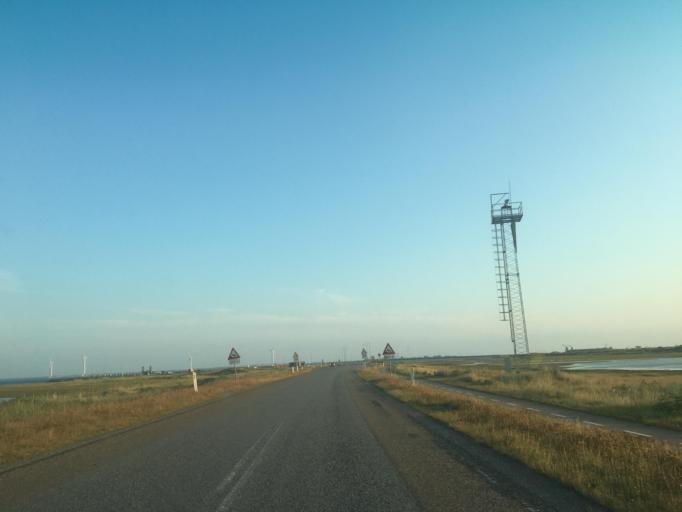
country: DK
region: Central Jutland
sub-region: Lemvig Kommune
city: Thyboron
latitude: 56.7065
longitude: 8.2474
